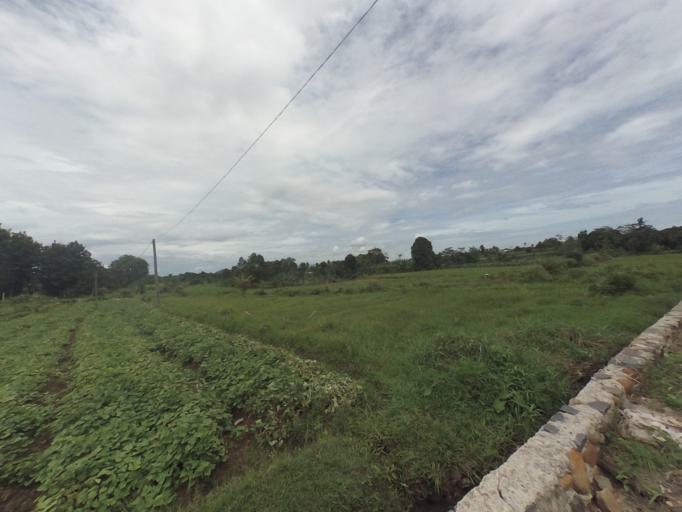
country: ID
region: West Java
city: Ciampea
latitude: -6.5492
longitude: 106.7384
